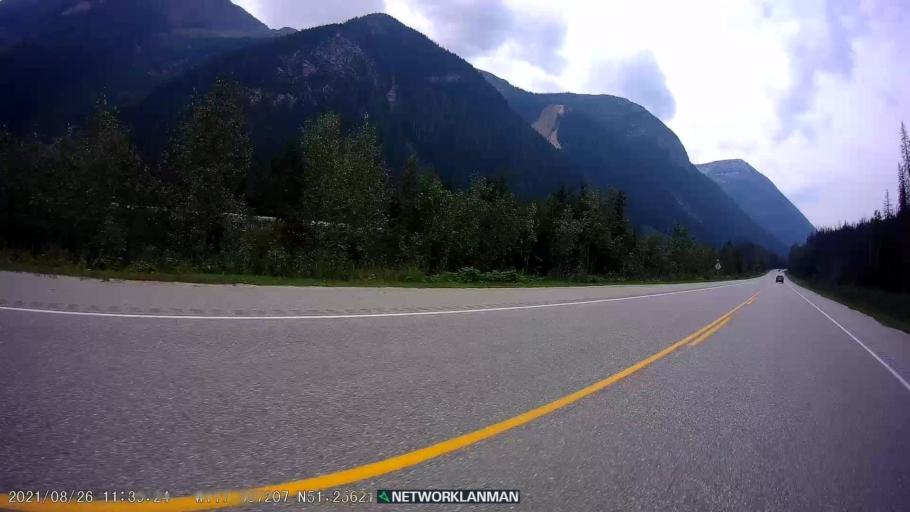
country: CA
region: British Columbia
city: Golden
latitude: 51.2561
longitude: -117.5878
